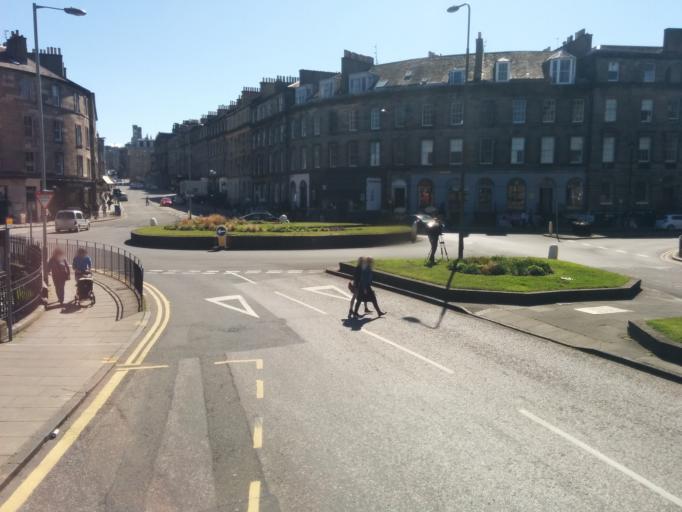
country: GB
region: Scotland
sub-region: Edinburgh
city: Edinburgh
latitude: 55.9597
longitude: -3.1912
